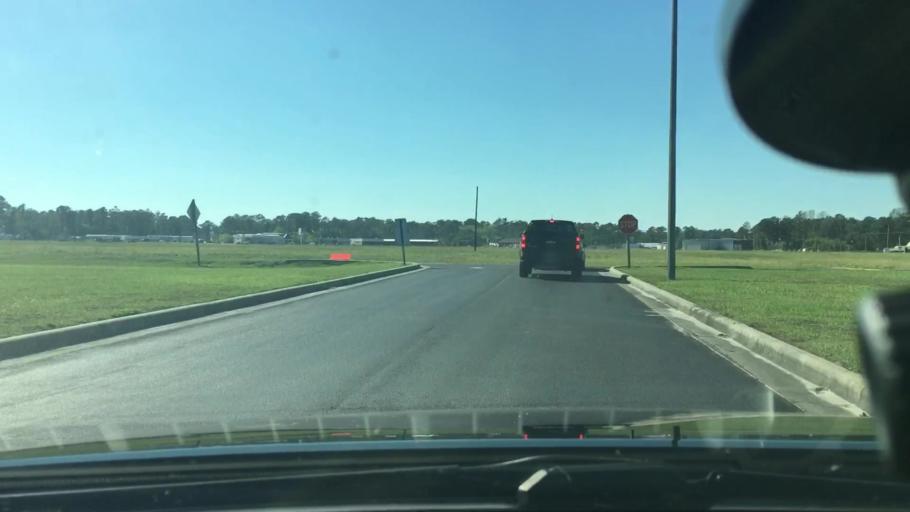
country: US
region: North Carolina
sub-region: Craven County
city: Havelock
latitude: 34.8809
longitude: -76.9002
